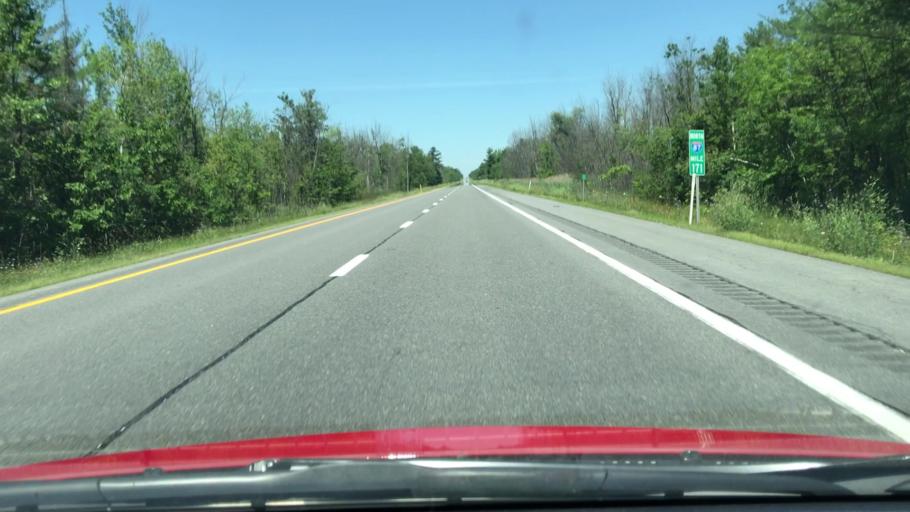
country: US
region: New York
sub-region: Clinton County
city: Champlain
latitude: 44.9373
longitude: -73.4468
